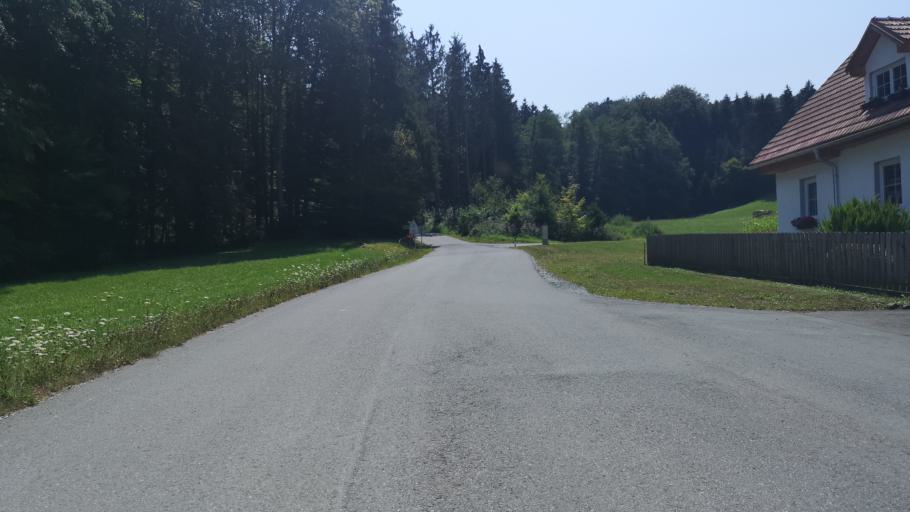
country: AT
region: Styria
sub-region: Politischer Bezirk Deutschlandsberg
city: Unterbergla
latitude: 46.8127
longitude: 15.2866
